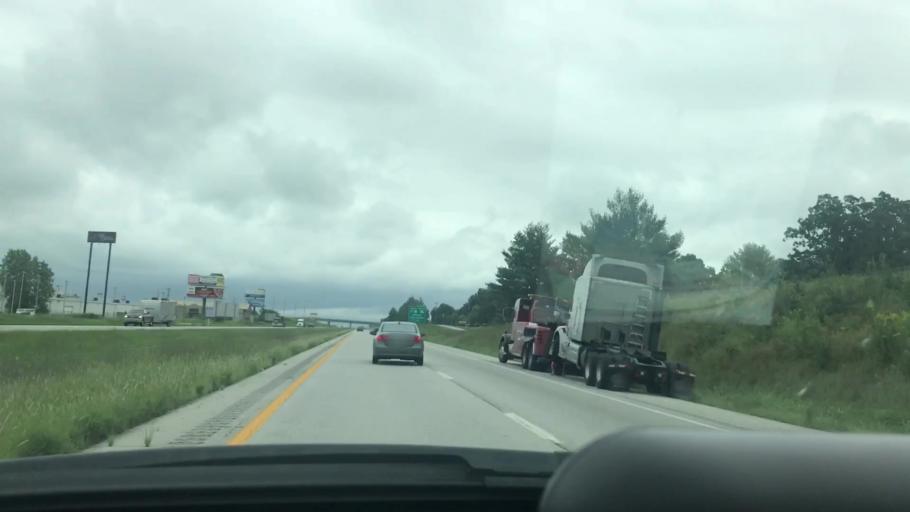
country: US
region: Missouri
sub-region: Jasper County
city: Duquesne
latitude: 37.0522
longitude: -94.4541
